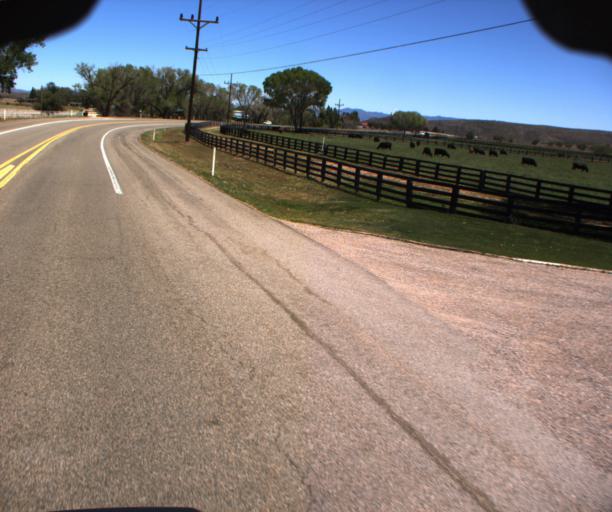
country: US
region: Arizona
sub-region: Yavapai County
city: Congress
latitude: 34.2741
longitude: -112.7272
